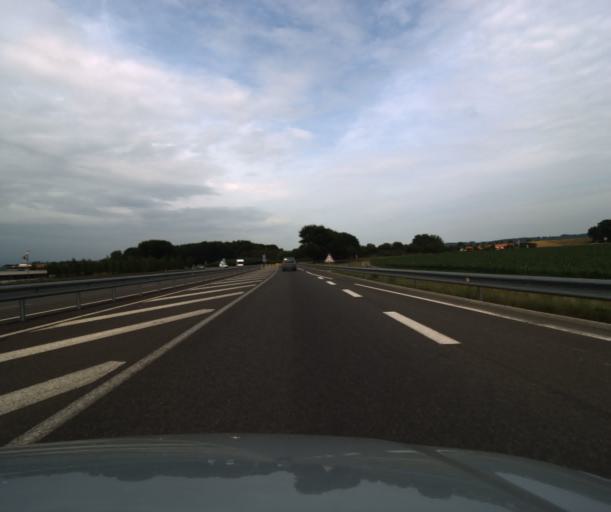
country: FR
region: Midi-Pyrenees
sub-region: Departement des Hautes-Pyrenees
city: Juillan
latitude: 43.2232
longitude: 0.0286
